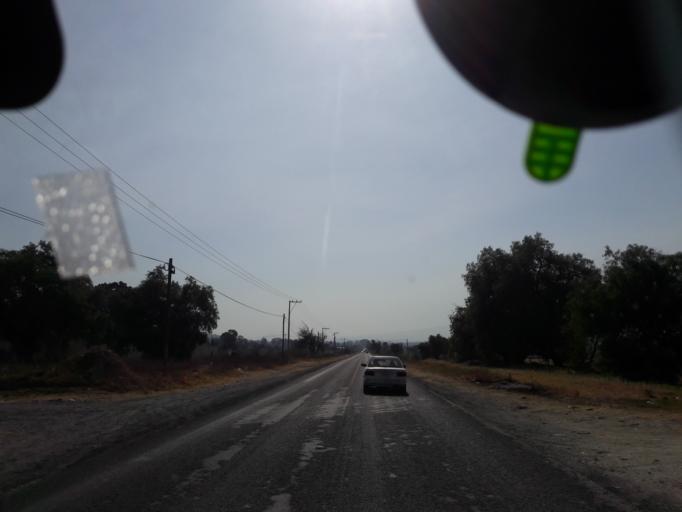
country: MX
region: Tlaxcala
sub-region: Panotla
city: Fraccionamiento la Virgen
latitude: 19.3211
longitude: -98.2954
